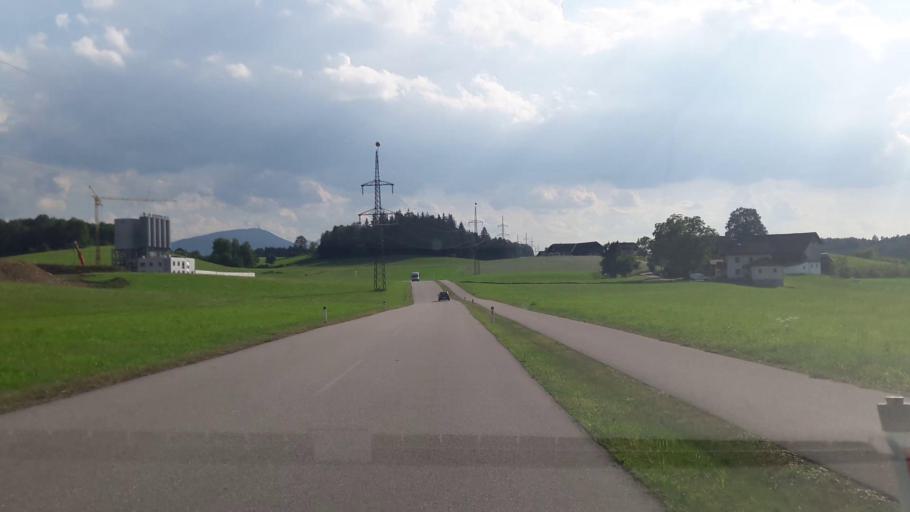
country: AT
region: Salzburg
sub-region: Politischer Bezirk Salzburg-Umgebung
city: Henndorf am Wallersee
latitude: 47.8902
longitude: 13.1905
